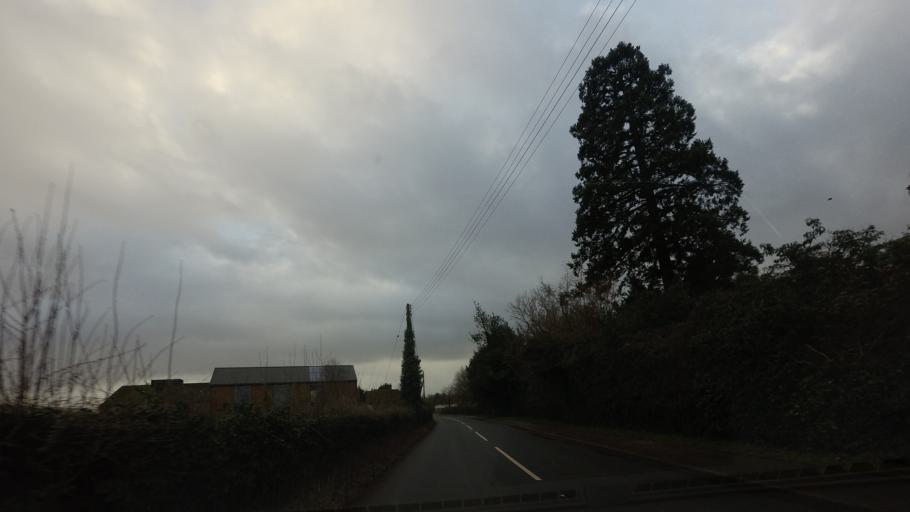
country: GB
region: England
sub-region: Kent
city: Yalding
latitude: 51.2194
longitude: 0.4309
